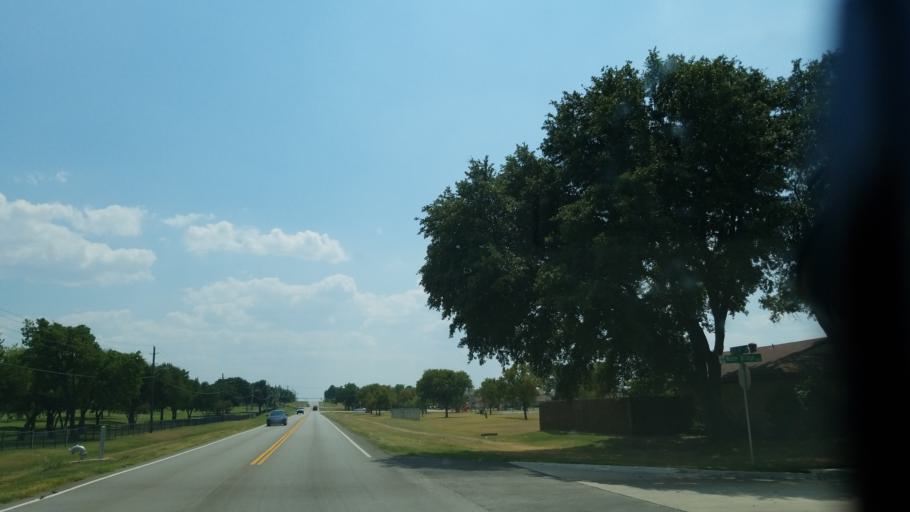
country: US
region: Texas
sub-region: Dallas County
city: Grand Prairie
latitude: 32.7006
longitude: -96.9851
